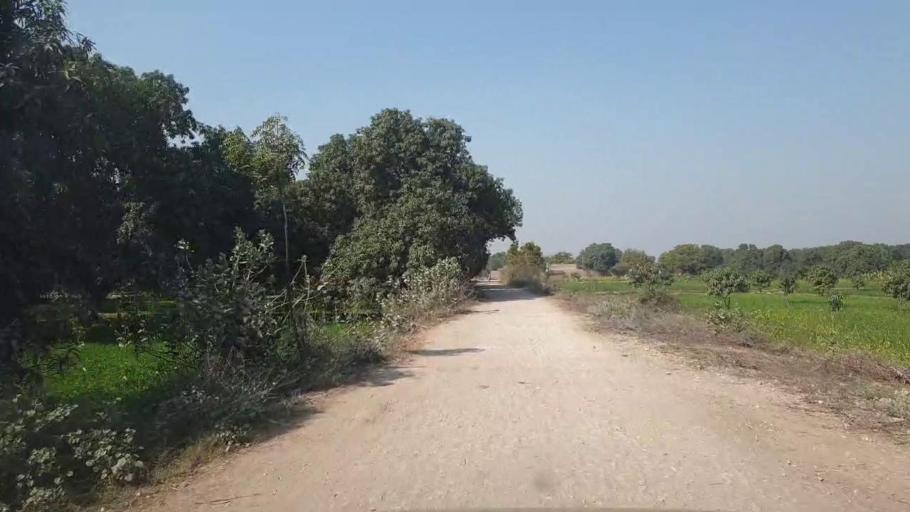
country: PK
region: Sindh
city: Tando Jam
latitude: 25.3299
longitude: 68.5969
